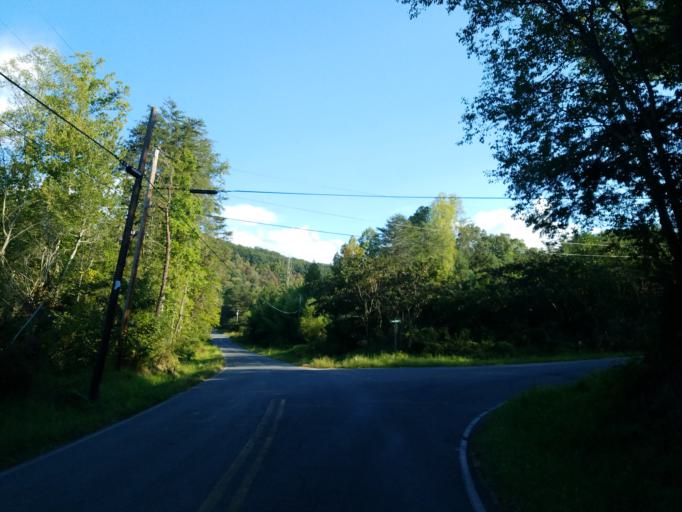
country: US
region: Georgia
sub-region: Murray County
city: Chatsworth
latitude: 34.9474
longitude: -84.7268
